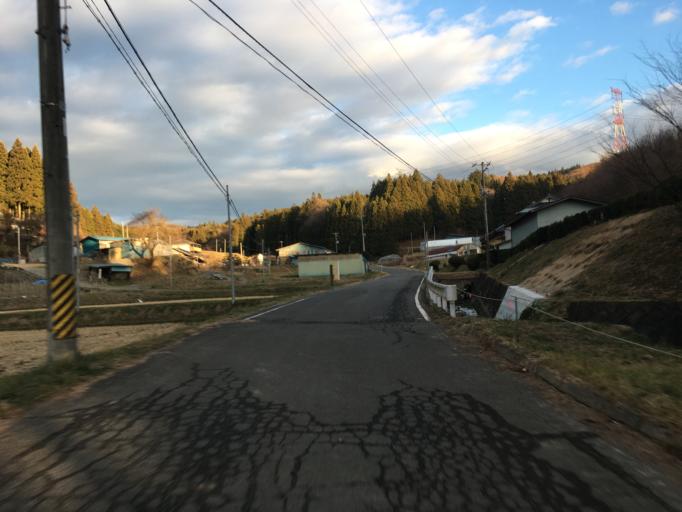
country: JP
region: Fukushima
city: Ishikawa
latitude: 37.1881
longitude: 140.5948
